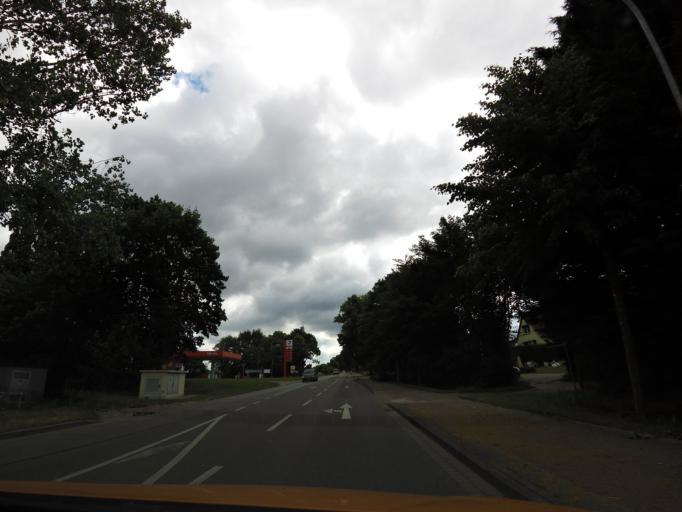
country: DE
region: Mecklenburg-Vorpommern
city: Guestrow
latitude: 53.7847
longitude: 12.1951
